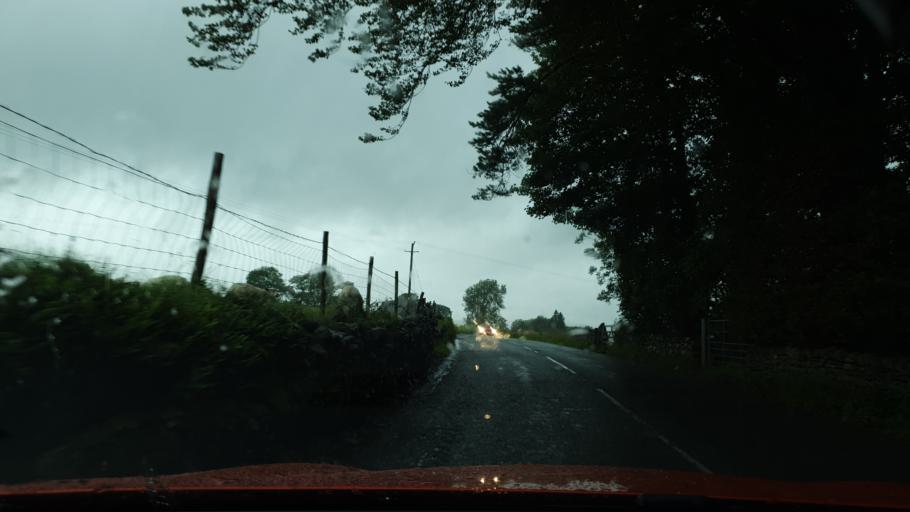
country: GB
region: England
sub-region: Cumbria
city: Ulverston
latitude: 54.2521
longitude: -3.0709
